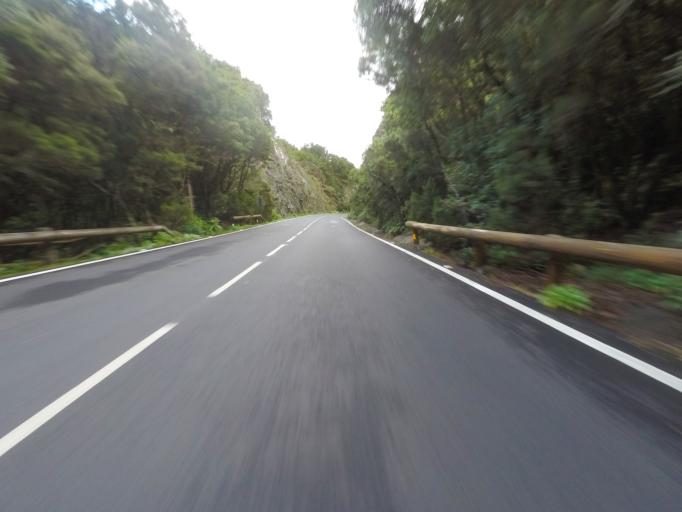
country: ES
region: Canary Islands
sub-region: Provincia de Santa Cruz de Tenerife
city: Alajero
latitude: 28.1117
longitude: -17.2176
